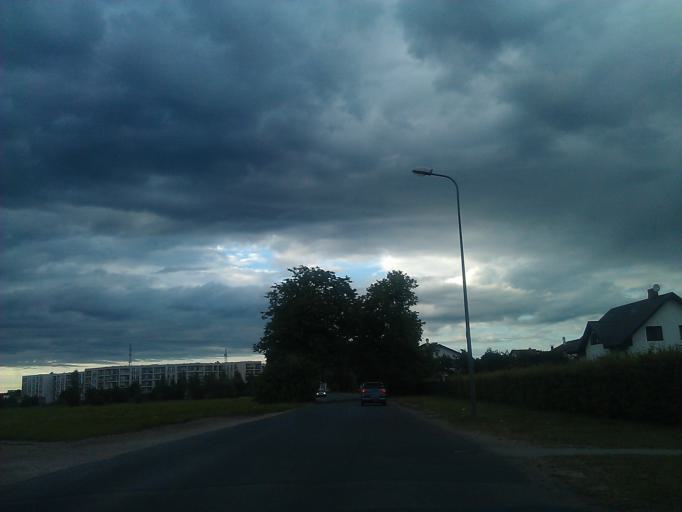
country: LV
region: Stopini
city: Ulbroka
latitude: 56.9519
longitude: 24.2439
